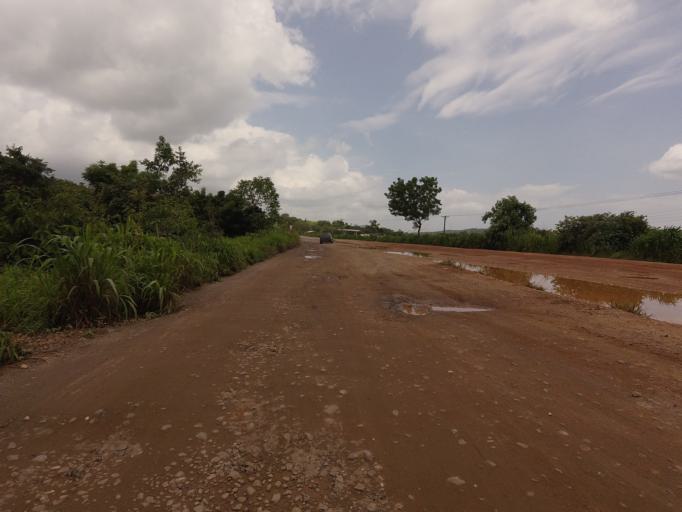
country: GH
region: Volta
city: Ho
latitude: 6.6772
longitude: 0.3147
